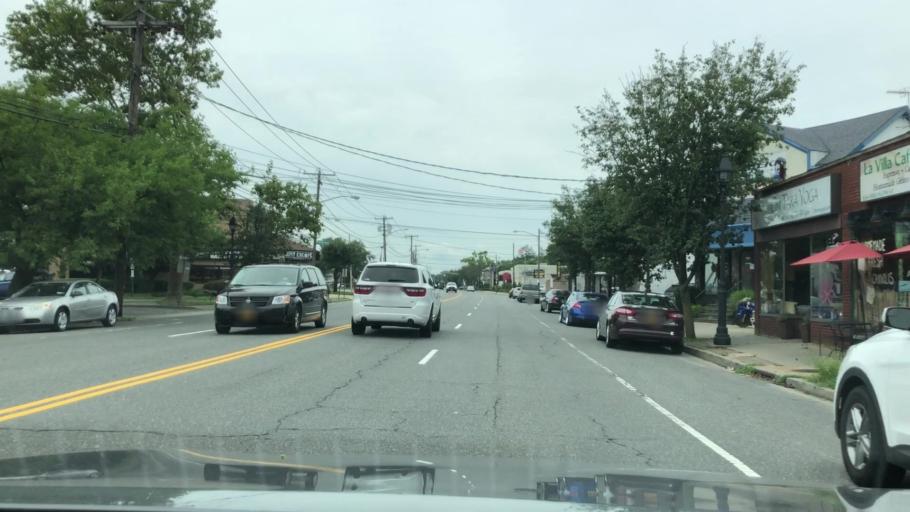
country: US
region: New York
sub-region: Nassau County
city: Massapequa
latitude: 40.6785
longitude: -73.4703
